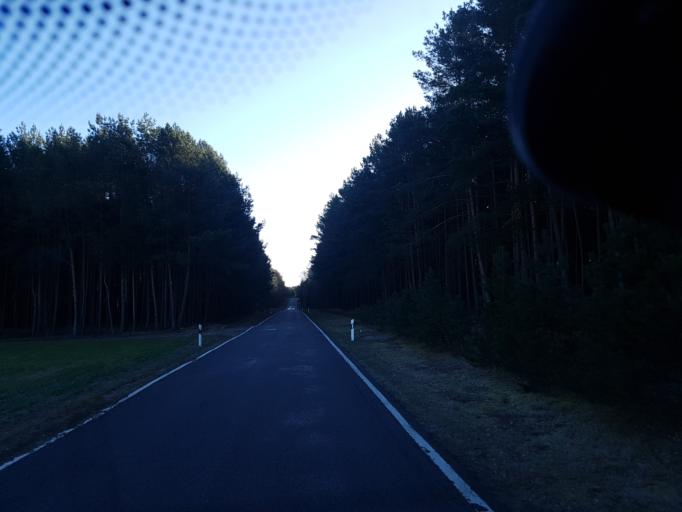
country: DE
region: Brandenburg
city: Jamlitz
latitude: 52.0402
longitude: 14.3775
